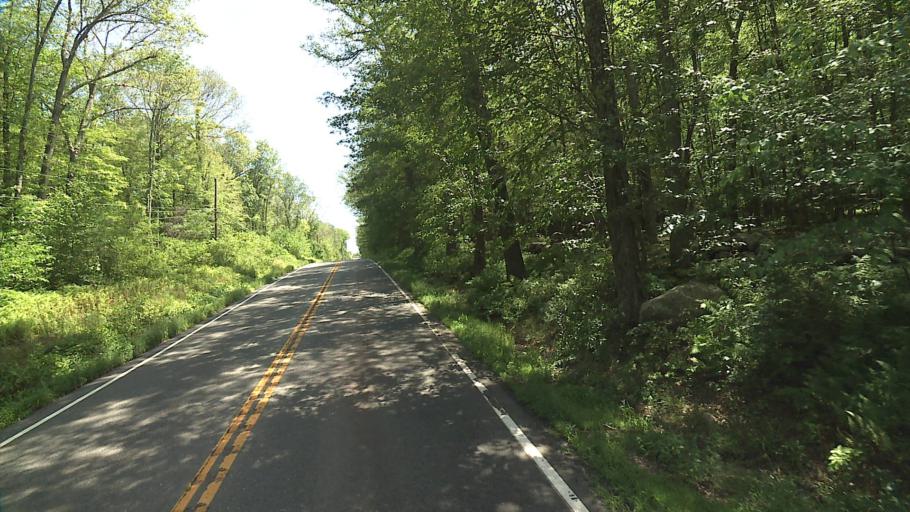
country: US
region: Connecticut
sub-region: Windham County
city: South Woodstock
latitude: 41.8989
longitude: -72.0081
